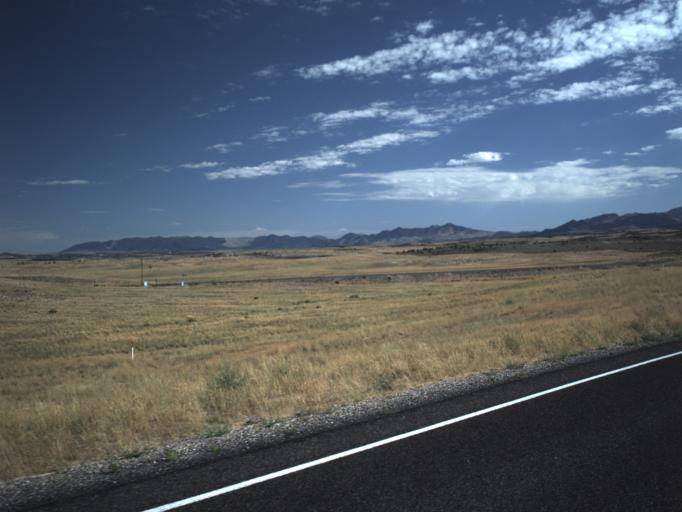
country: US
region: Utah
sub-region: Juab County
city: Mona
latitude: 39.7047
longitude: -112.2135
